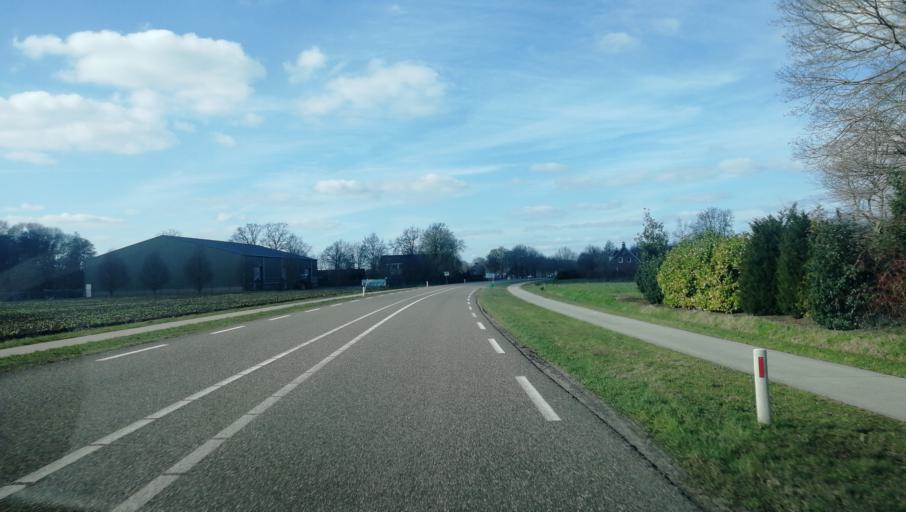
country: NL
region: Limburg
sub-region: Gemeente Peel en Maas
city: Maasbree
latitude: 51.4056
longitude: 6.0570
